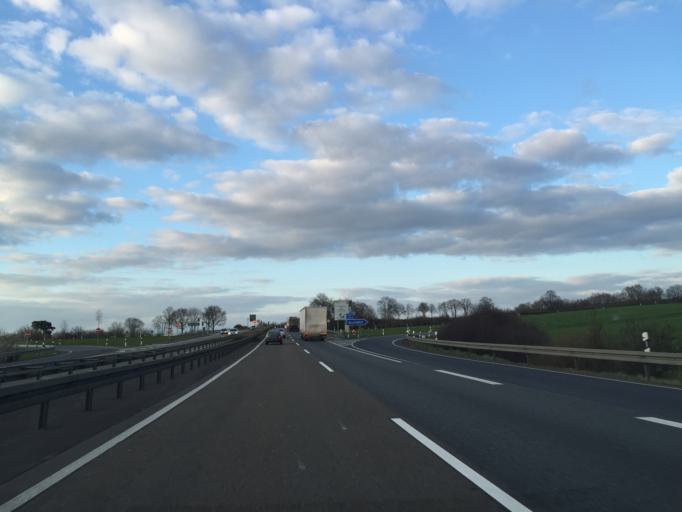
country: DE
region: Hesse
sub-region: Regierungsbezirk Giessen
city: Alsfeld
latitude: 50.7473
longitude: 9.2976
